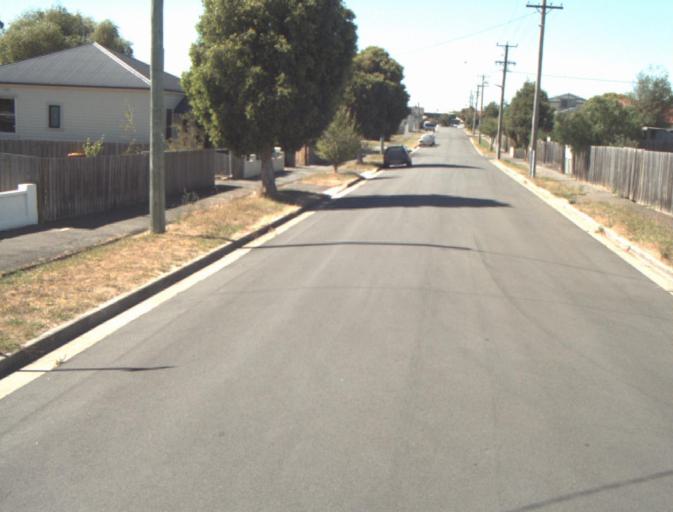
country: AU
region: Tasmania
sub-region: Launceston
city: Newnham
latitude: -41.4146
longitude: 147.1380
